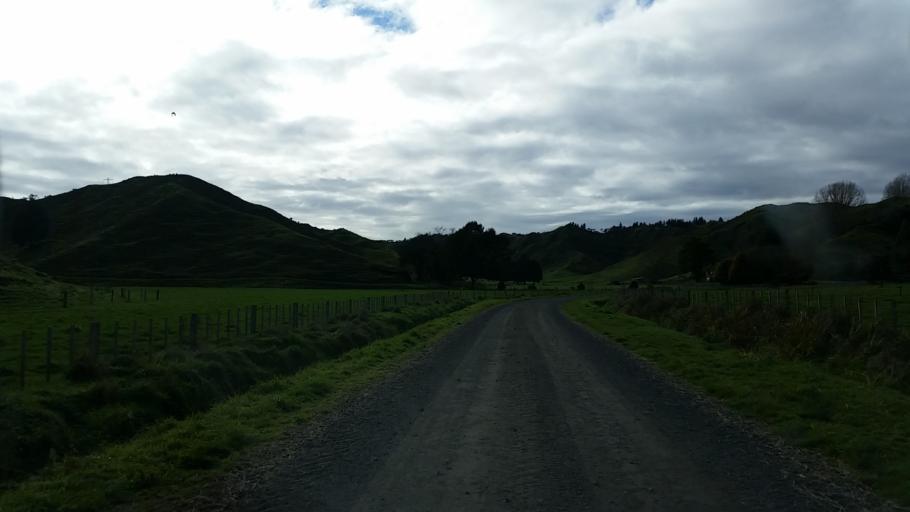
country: NZ
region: Taranaki
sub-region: South Taranaki District
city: Eltham
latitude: -39.2505
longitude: 174.5377
